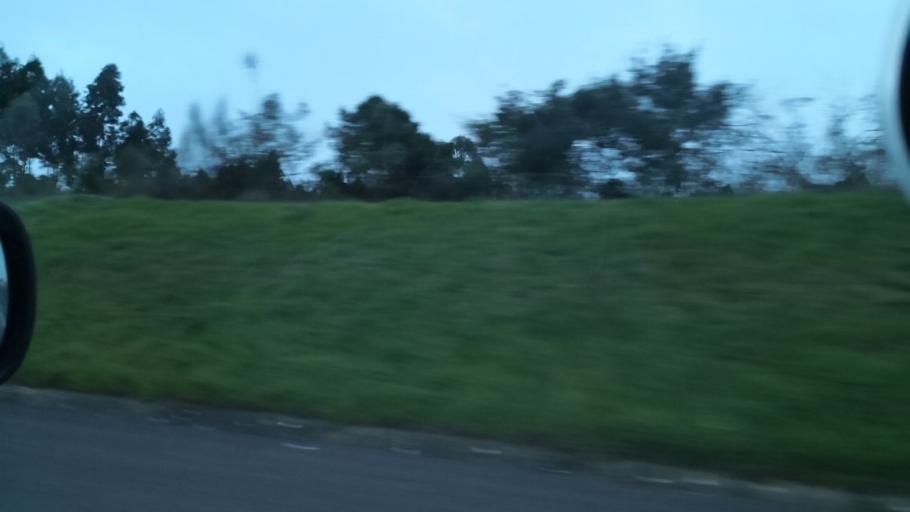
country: PT
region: Aveiro
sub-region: Mealhada
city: Pampilhosa do Botao
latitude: 40.2966
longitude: -8.4861
